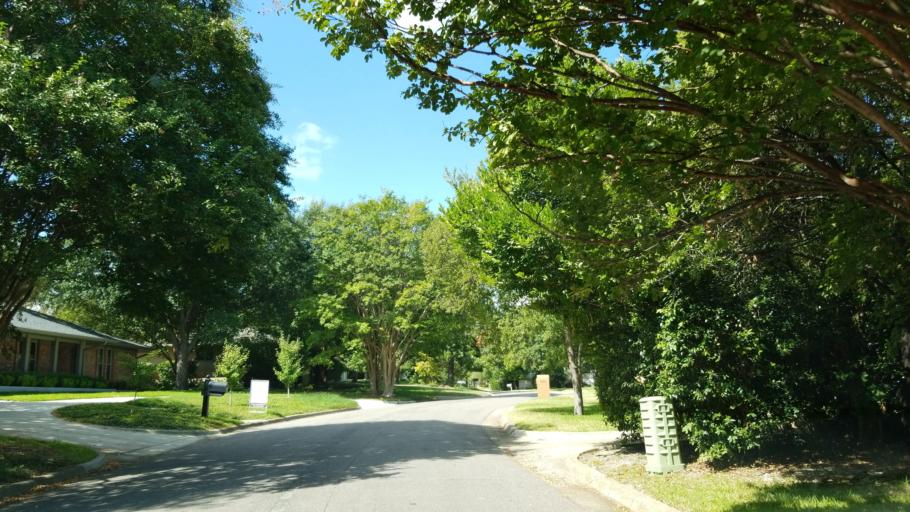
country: US
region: Texas
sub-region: Dallas County
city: Addison
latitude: 32.9310
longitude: -96.7979
